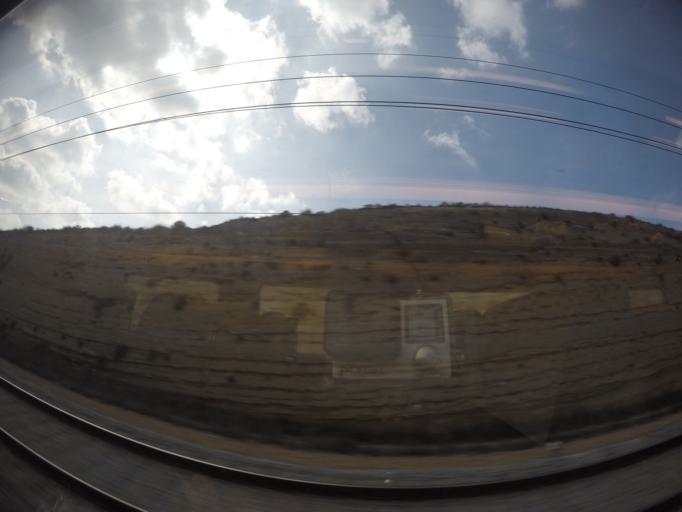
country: ES
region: Aragon
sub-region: Provincia de Zaragoza
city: El Burgo de Ebro
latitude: 41.5568
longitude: -0.7643
